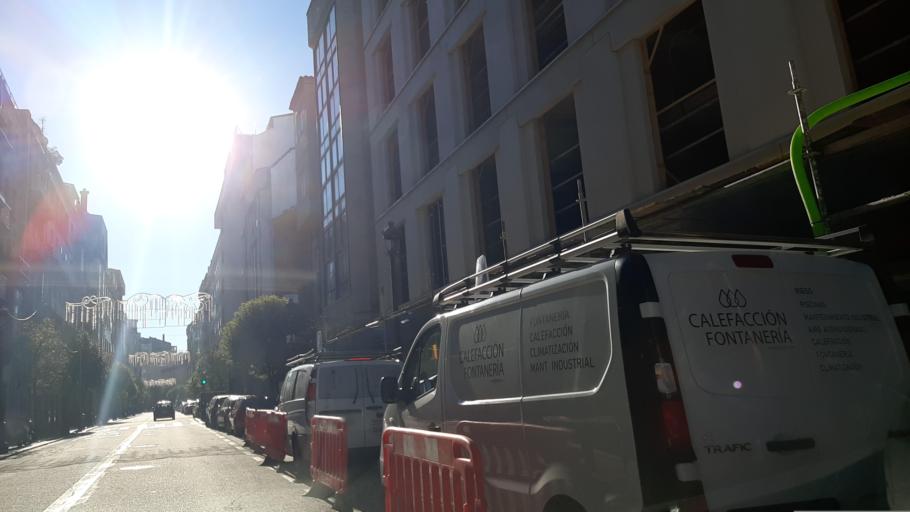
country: ES
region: Galicia
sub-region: Provincia de Pontevedra
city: Vigo
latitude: 42.2347
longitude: -8.7295
